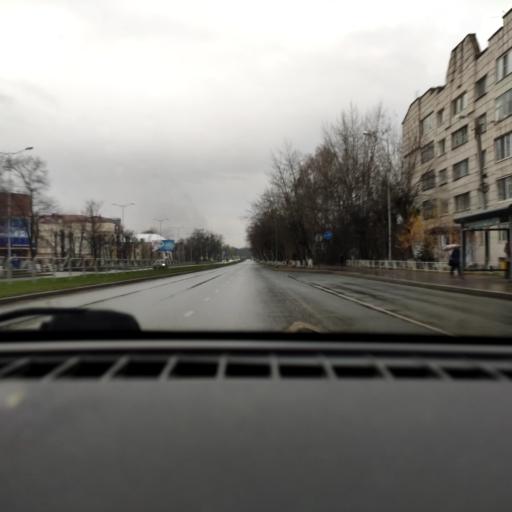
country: RU
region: Perm
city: Kultayevo
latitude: 58.0013
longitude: 55.9449
